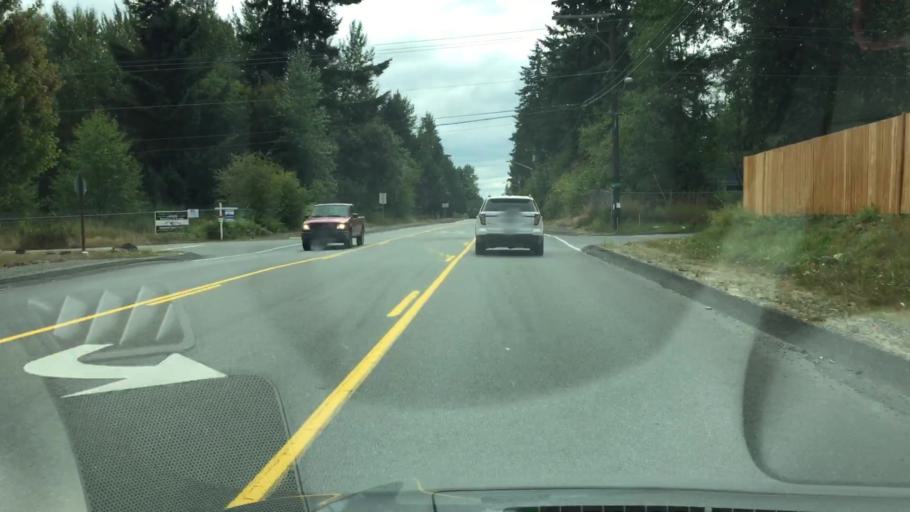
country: US
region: Washington
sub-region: Pierce County
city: South Hill
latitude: 47.1076
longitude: -122.2668
